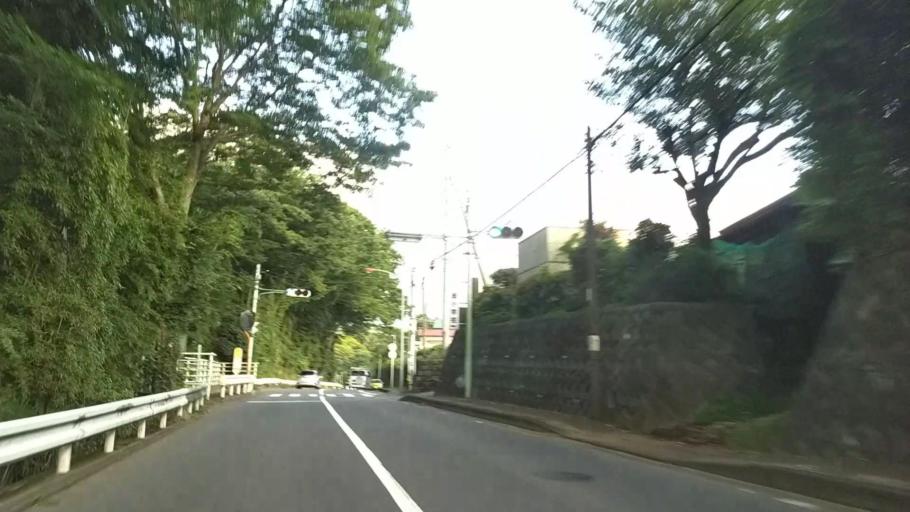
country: JP
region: Kanagawa
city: Atsugi
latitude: 35.4815
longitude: 139.2777
